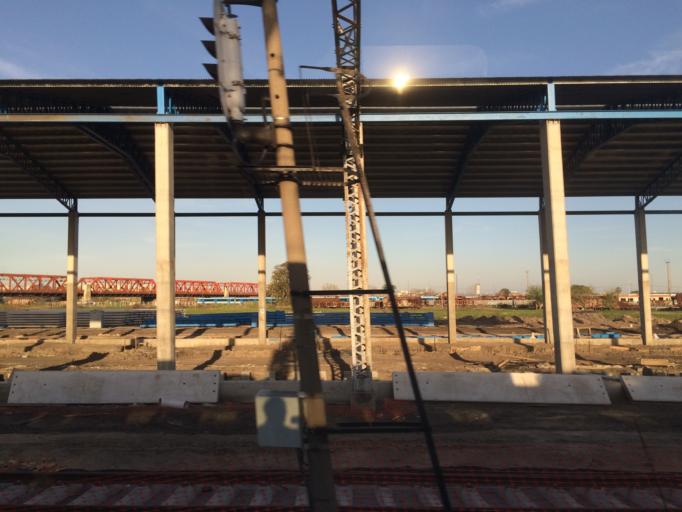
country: AR
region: Buenos Aires
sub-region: Partido de Avellaneda
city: Avellaneda
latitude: -34.6737
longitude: -58.3782
